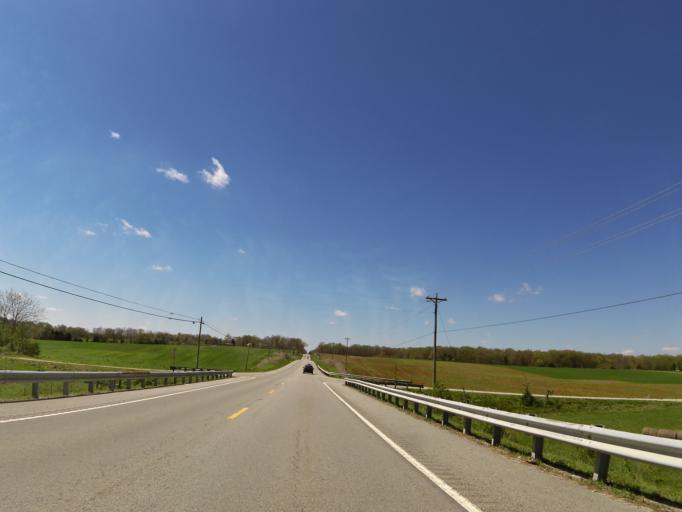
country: US
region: Tennessee
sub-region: White County
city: Sparta
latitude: 35.9503
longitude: -85.5448
